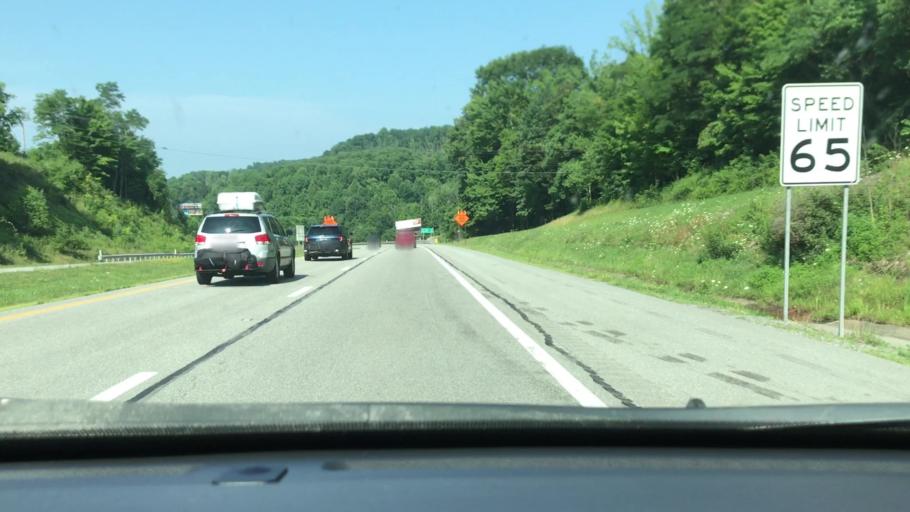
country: US
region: West Virginia
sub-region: Nicholas County
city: Summersville
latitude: 38.2676
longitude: -80.8453
